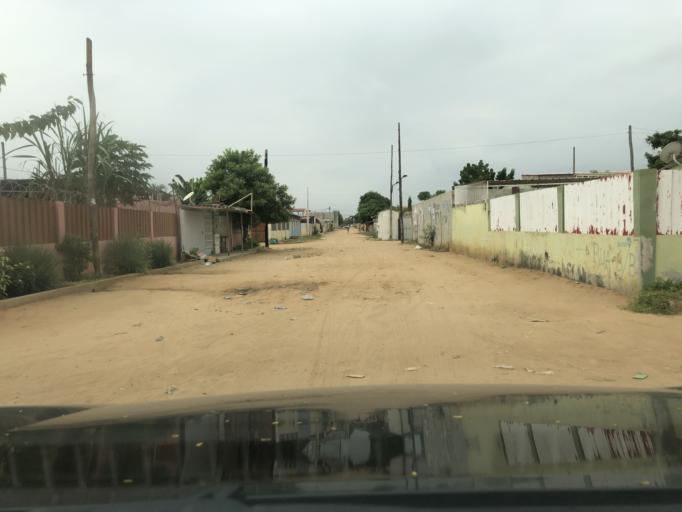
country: AO
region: Luanda
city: Luanda
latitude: -8.9360
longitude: 13.2533
